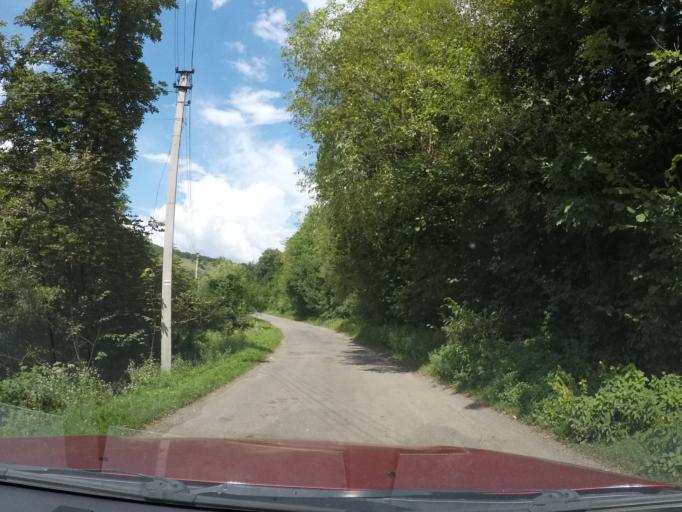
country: UA
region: Zakarpattia
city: Velykyi Bereznyi
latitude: 49.0125
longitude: 22.6255
